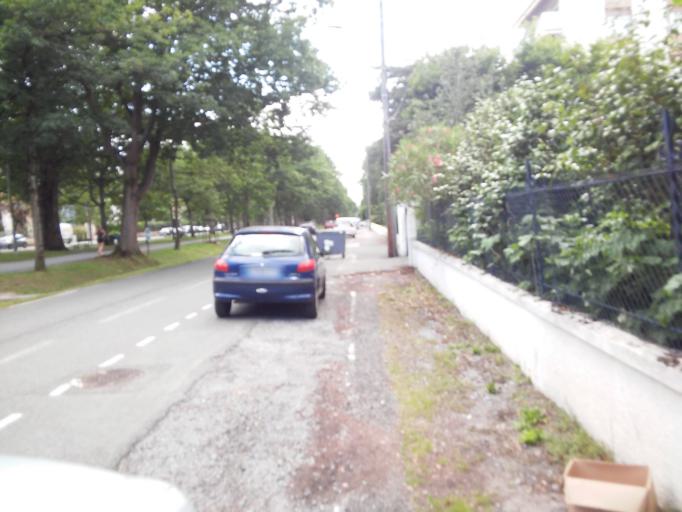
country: FR
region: Aquitaine
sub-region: Departement des Pyrenees-Atlantiques
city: Bizanos
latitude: 43.3075
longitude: -0.3409
